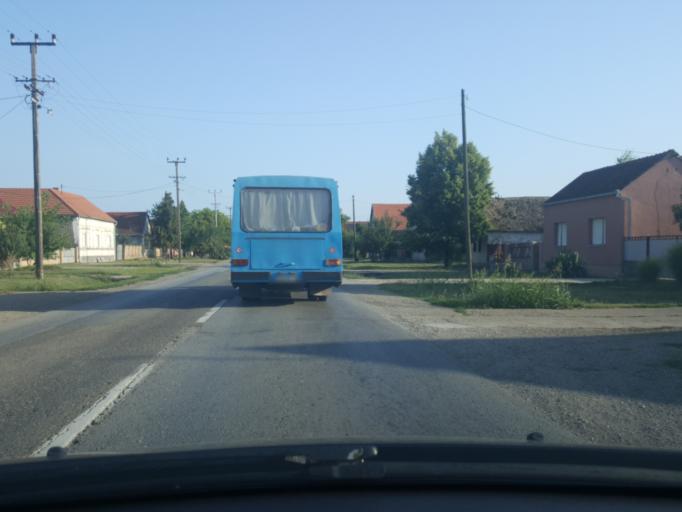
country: RS
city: Hrtkovci
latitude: 44.8748
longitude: 19.7692
